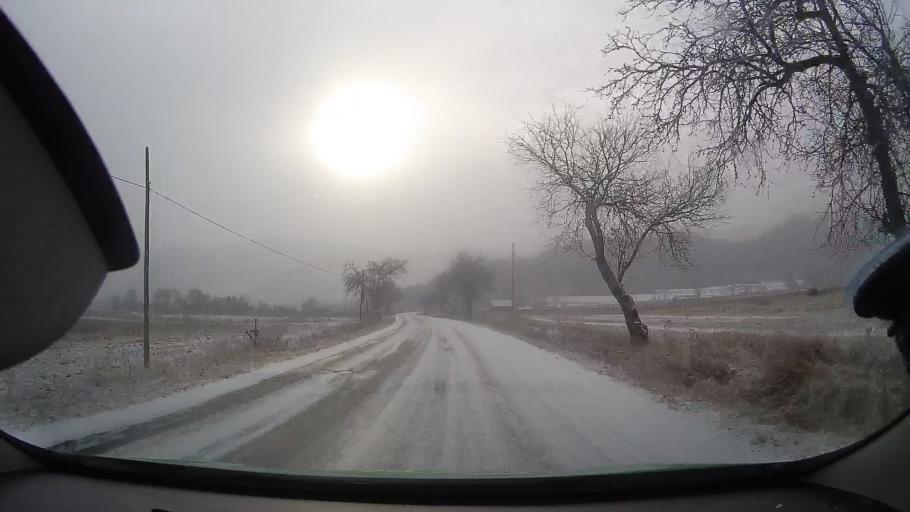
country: RO
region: Alba
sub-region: Comuna Rimetea
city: Rimetea
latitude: 46.3969
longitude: 23.5601
